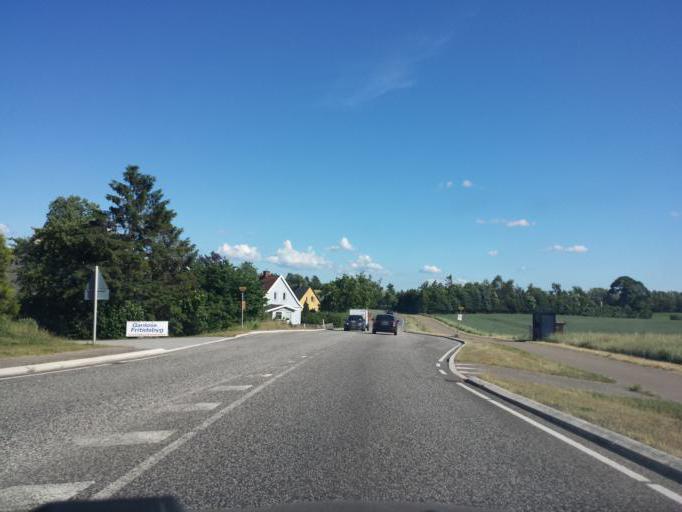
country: DK
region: Capital Region
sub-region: Egedal Kommune
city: Ganlose
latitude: 55.7824
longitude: 12.2804
